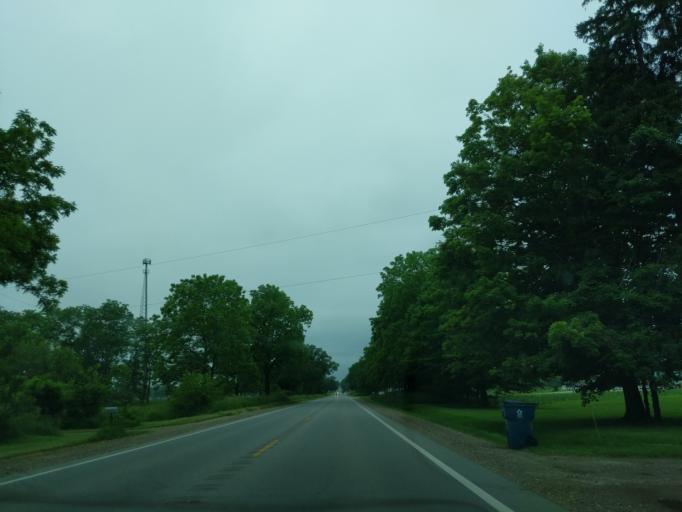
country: US
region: Michigan
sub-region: Branch County
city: Quincy
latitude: 41.9485
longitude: -84.8173
